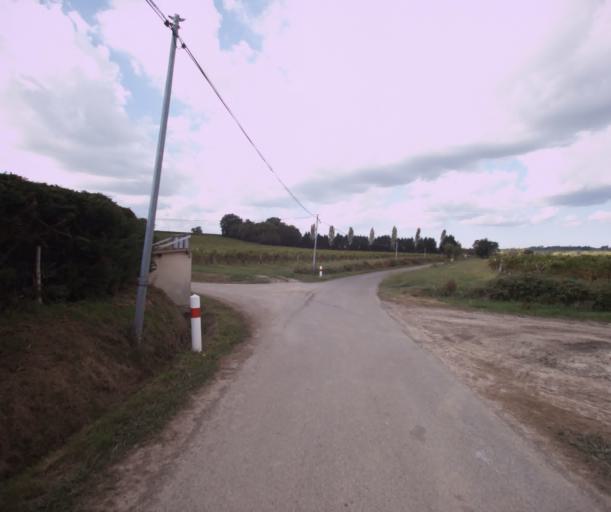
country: FR
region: Midi-Pyrenees
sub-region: Departement du Gers
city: Cazaubon
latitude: 43.8975
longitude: -0.0491
